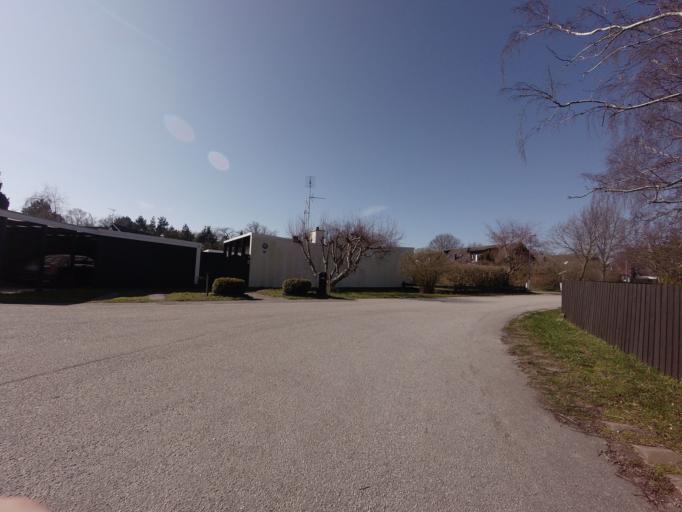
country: SE
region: Skane
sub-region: Vellinge Kommun
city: Skanor med Falsterbo
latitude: 55.3938
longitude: 12.8448
